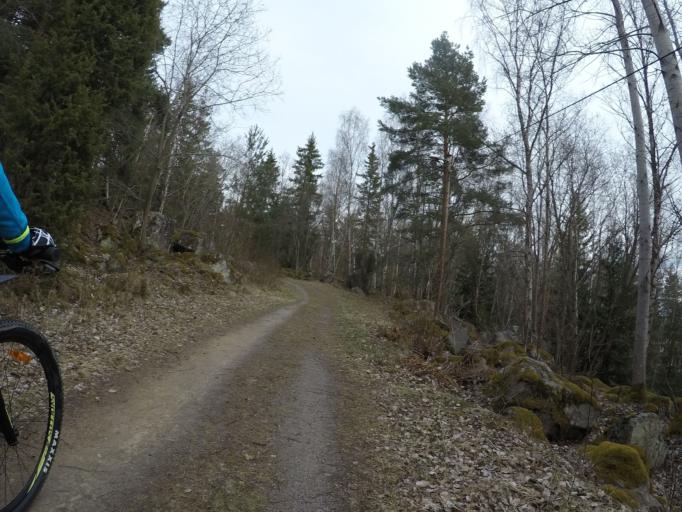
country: SE
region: Soedermanland
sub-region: Eskilstuna Kommun
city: Torshalla
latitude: 59.4242
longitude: 16.4929
